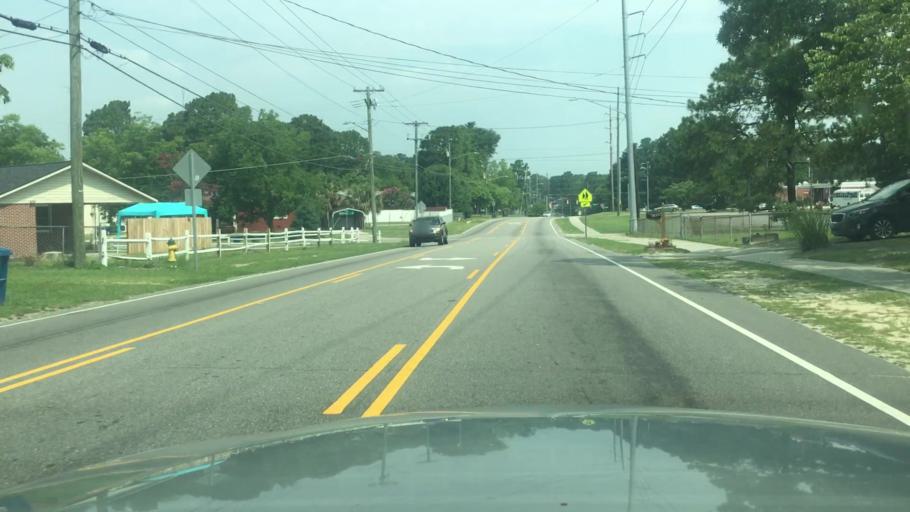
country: US
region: North Carolina
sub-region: Cumberland County
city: Hope Mills
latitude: 35.0235
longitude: -78.9413
